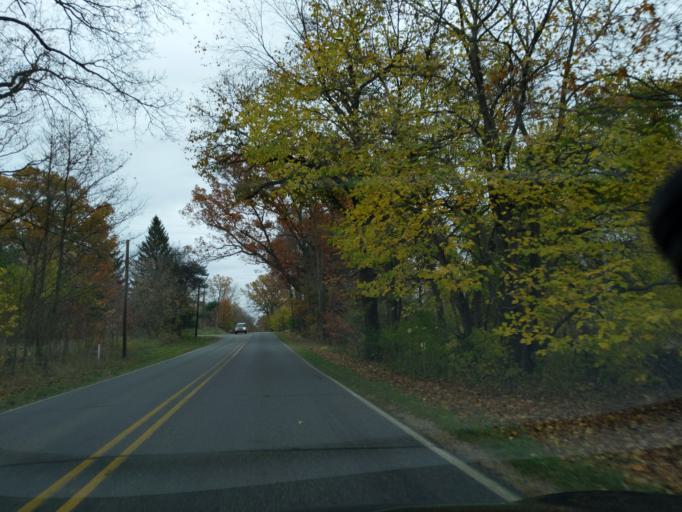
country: US
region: Michigan
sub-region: Jackson County
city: Spring Arbor
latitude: 42.2767
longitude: -84.5729
